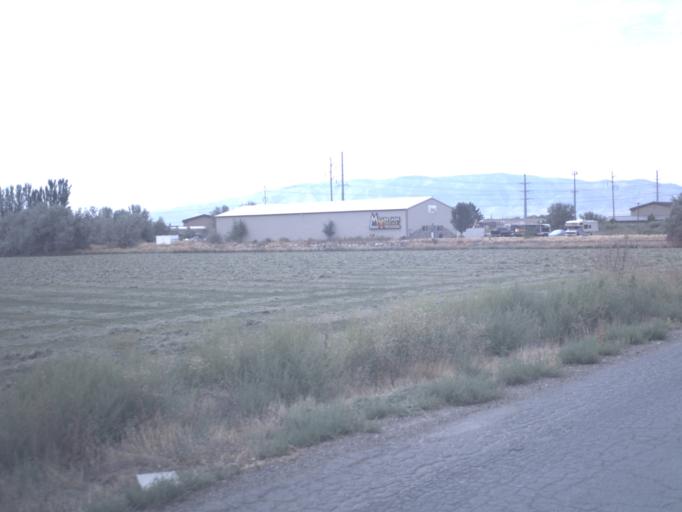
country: US
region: Utah
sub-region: Utah County
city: American Fork
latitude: 40.3477
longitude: -111.7758
